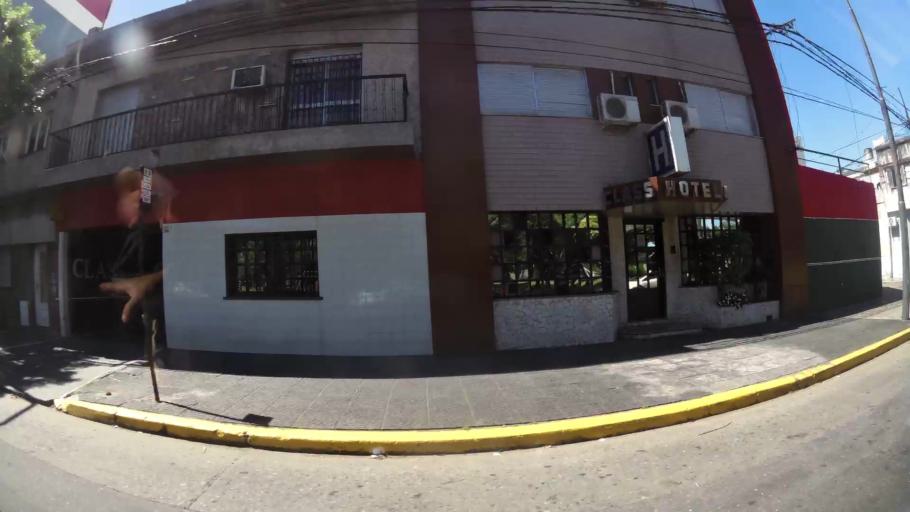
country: AR
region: Santa Fe
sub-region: Departamento de Rosario
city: Rosario
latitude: -32.9383
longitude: -60.6757
